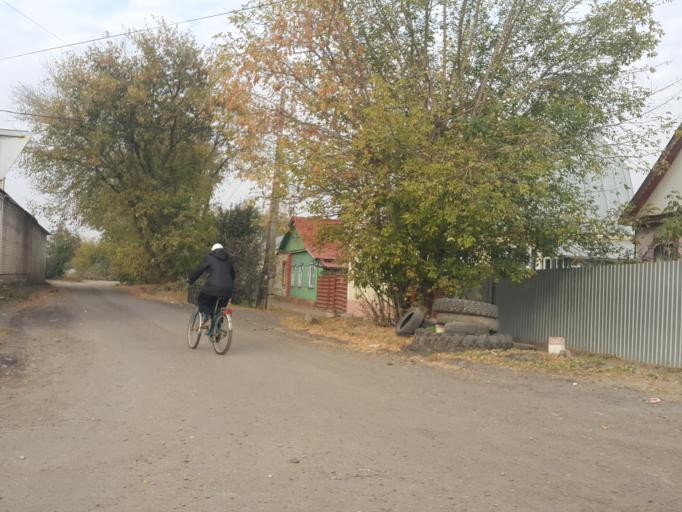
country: RU
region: Tambov
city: Tambov
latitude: 52.6994
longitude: 41.4625
